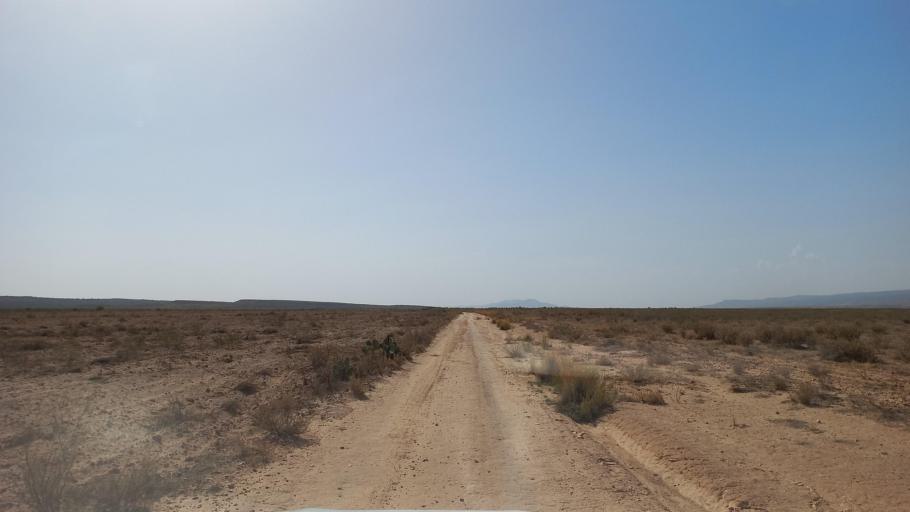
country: TN
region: Al Qasrayn
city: Kasserine
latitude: 35.2170
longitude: 9.0300
